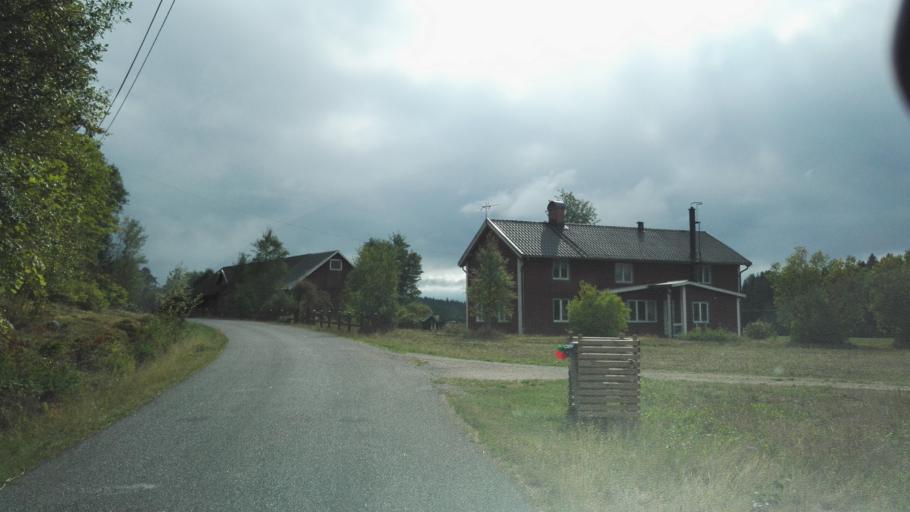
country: SE
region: Joenkoeping
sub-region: Vetlanda Kommun
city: Landsbro
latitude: 57.2235
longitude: 14.9673
